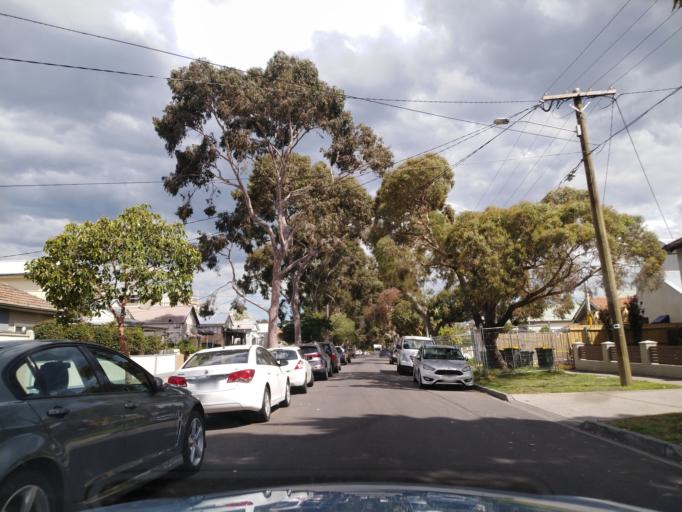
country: AU
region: Victoria
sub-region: Hobsons Bay
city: South Kingsville
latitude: -37.8380
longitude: 144.8769
